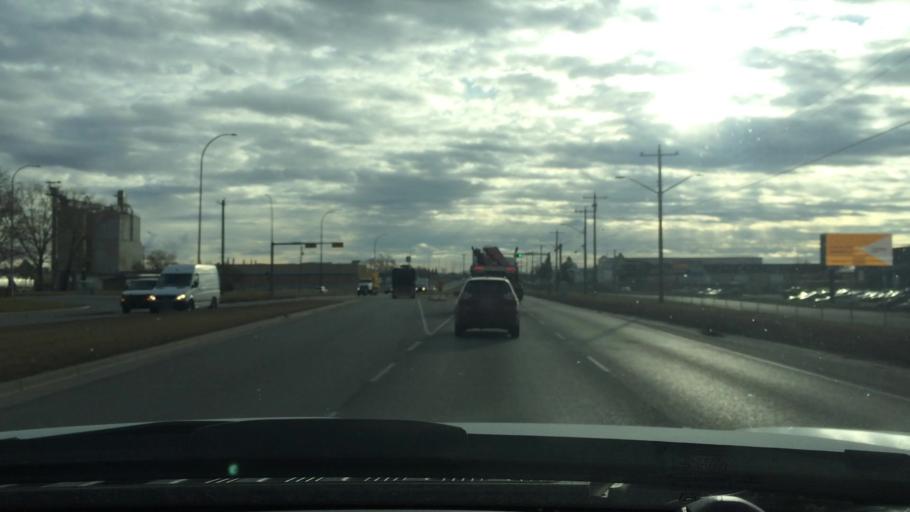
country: CA
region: Alberta
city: Calgary
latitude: 51.0050
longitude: -113.9959
